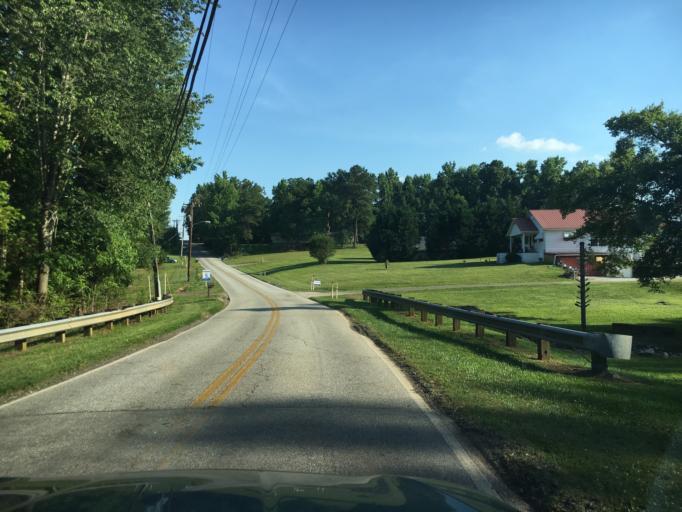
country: US
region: South Carolina
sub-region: Spartanburg County
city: Duncan
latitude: 34.8584
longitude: -82.1102
